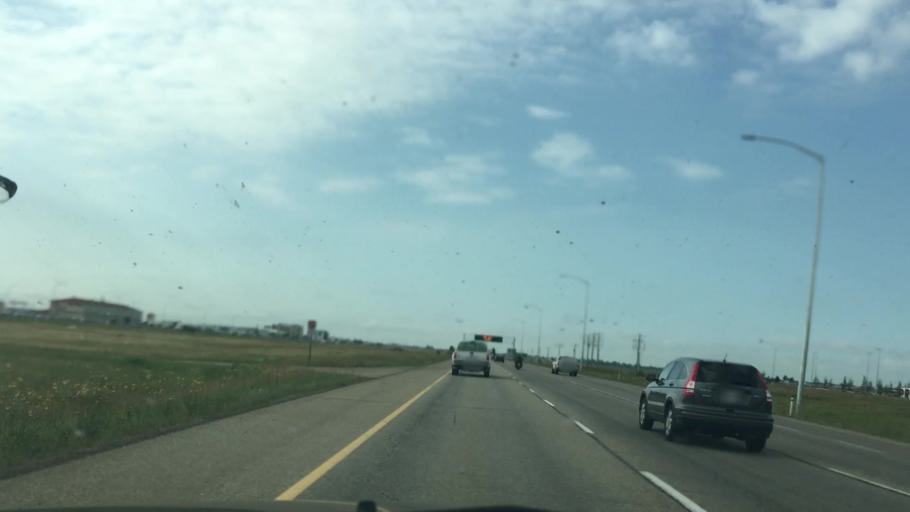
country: CA
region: Alberta
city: Leduc
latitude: 53.3029
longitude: -113.5499
